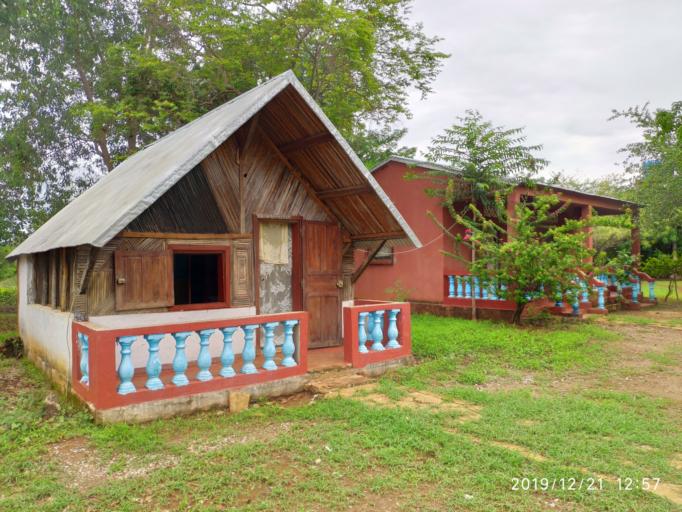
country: MG
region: Diana
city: Ambilobe
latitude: -12.9686
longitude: 49.1371
